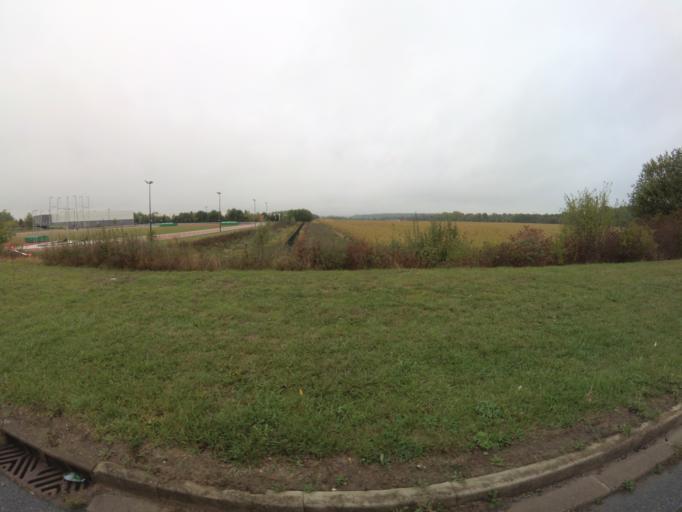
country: FR
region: Ile-de-France
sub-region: Departement de Seine-et-Marne
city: Chanteloup-en-Brie
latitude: 48.8438
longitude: 2.7420
